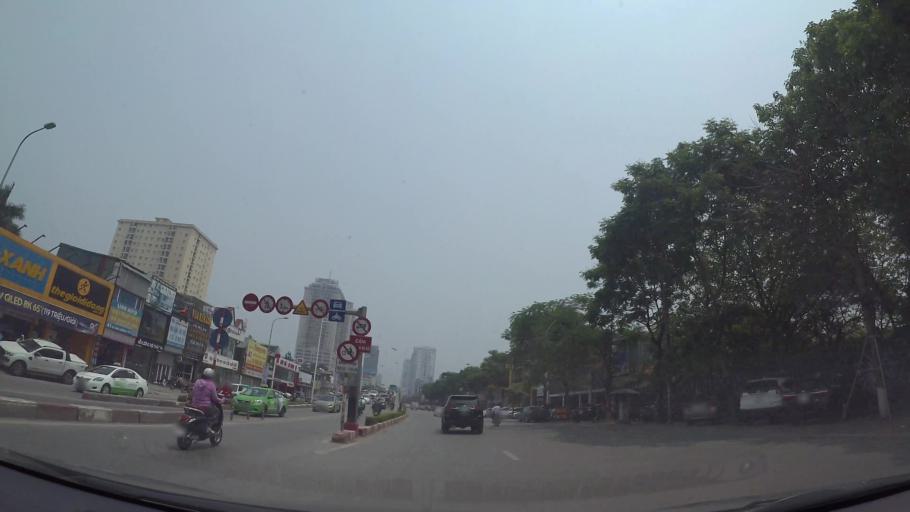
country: VN
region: Ha Noi
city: Thanh Xuan
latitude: 21.0088
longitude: 105.8095
